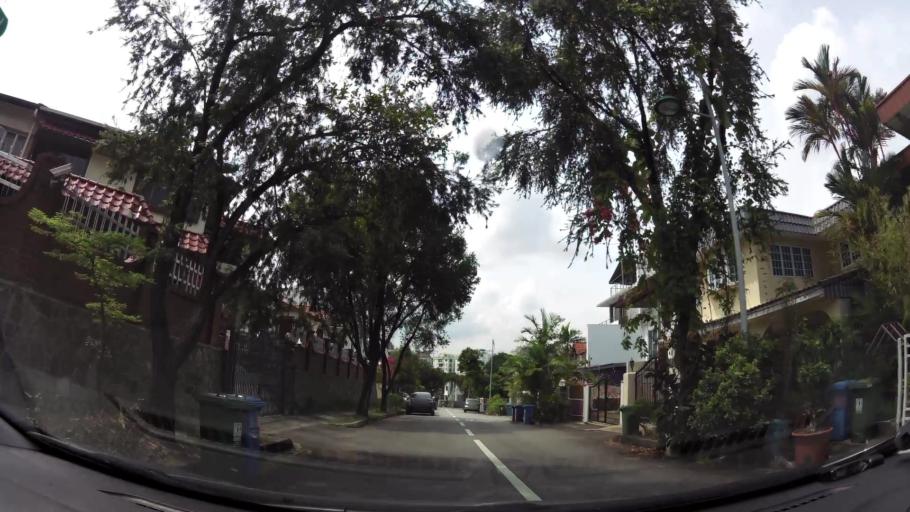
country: SG
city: Singapore
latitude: 1.3449
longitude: 103.7715
